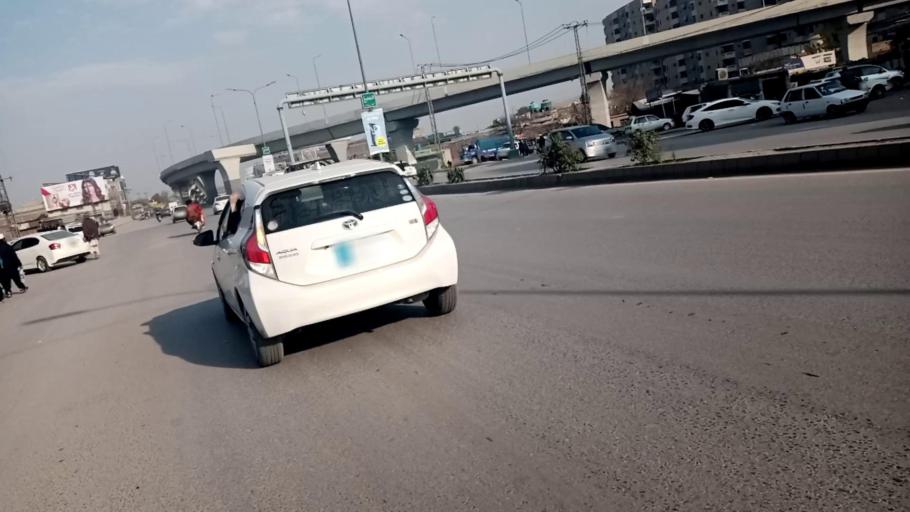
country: PK
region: Khyber Pakhtunkhwa
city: Peshawar
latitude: 33.9969
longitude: 71.4633
